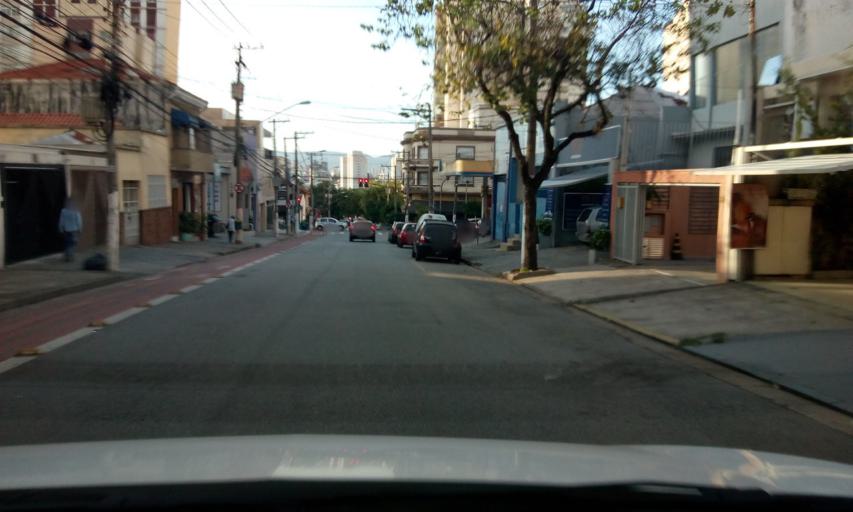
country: BR
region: Sao Paulo
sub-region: Sao Paulo
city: Sao Paulo
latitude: -23.5258
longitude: -46.6943
